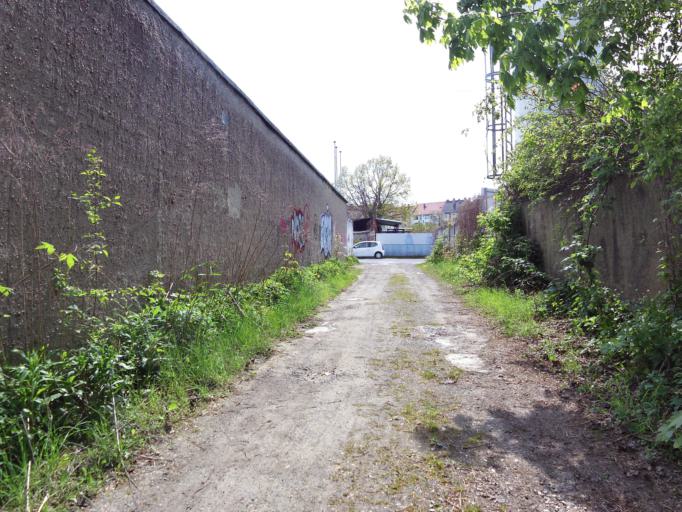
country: DE
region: Saxony
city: Leipzig
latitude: 51.3670
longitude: 12.3927
